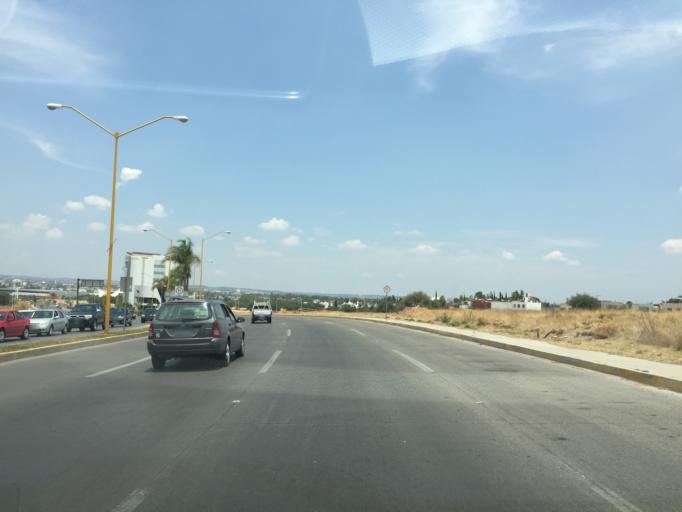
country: MX
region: Aguascalientes
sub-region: Aguascalientes
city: La Loma de los Negritos
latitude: 21.8636
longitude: -102.3346
